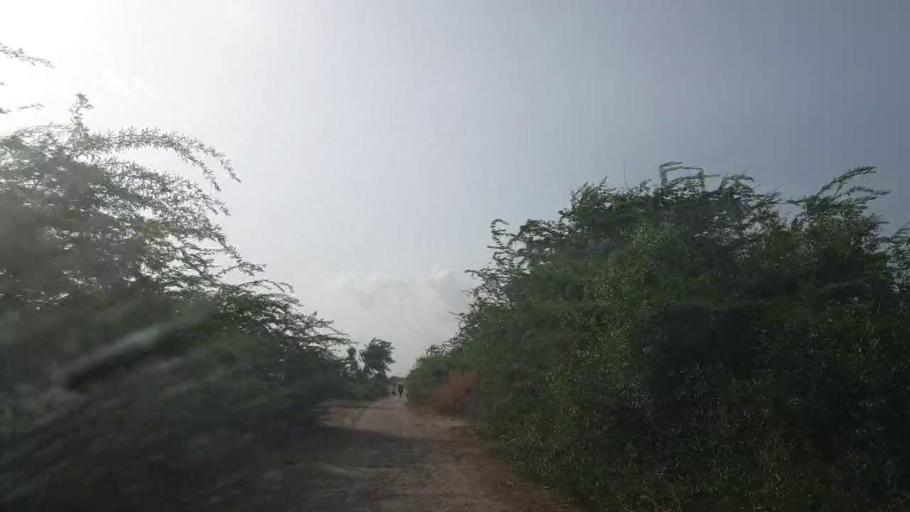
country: PK
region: Sindh
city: Tando Bago
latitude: 24.7588
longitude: 69.0827
